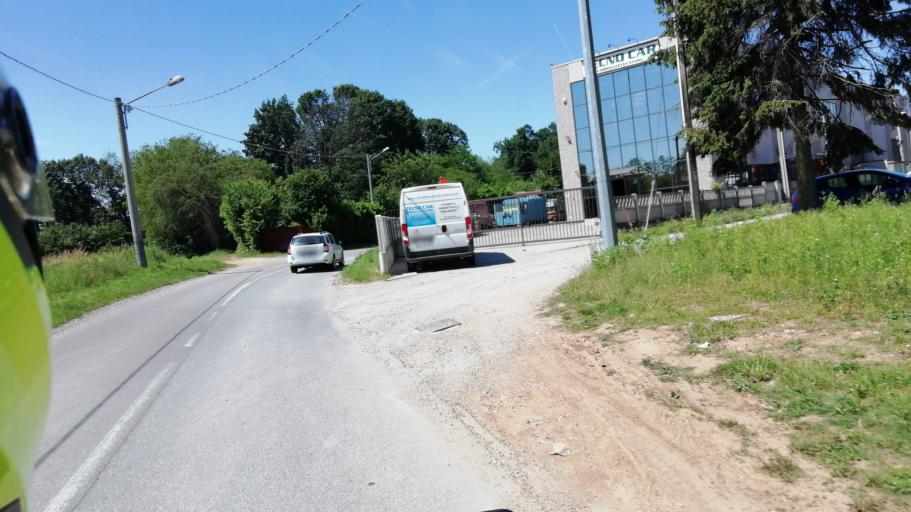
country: IT
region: Lombardy
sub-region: Provincia di Varese
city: Ferno
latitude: 45.6185
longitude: 8.7461
